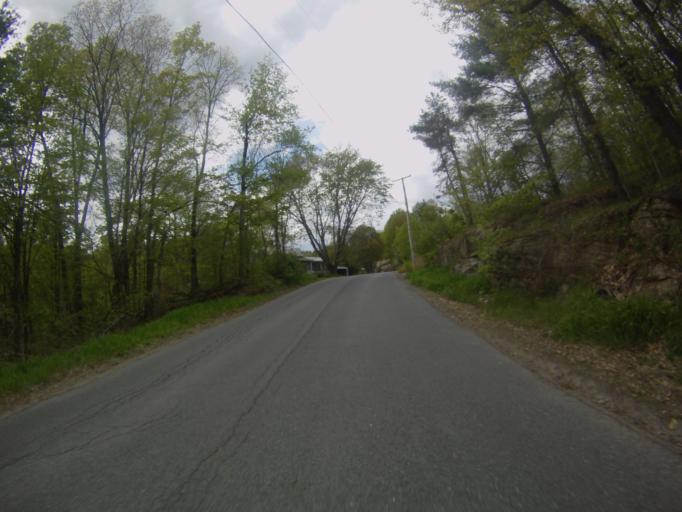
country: US
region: New York
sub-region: Essex County
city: Ticonderoga
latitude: 43.8821
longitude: -73.4721
